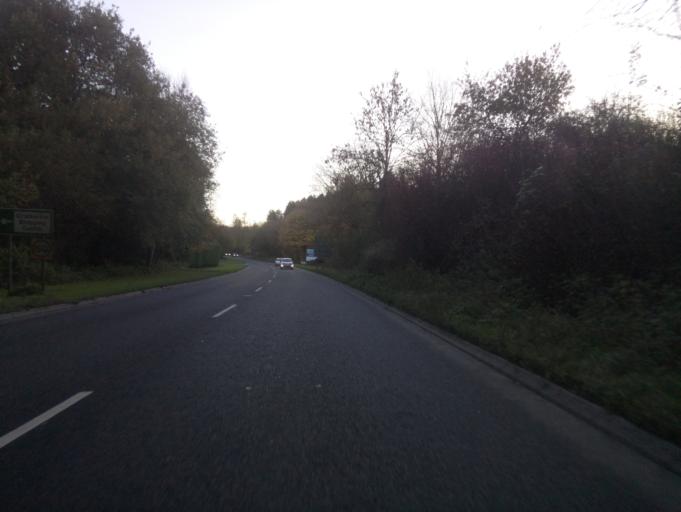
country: GB
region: England
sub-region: Wiltshire
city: Warminster
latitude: 51.1813
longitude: -2.1942
